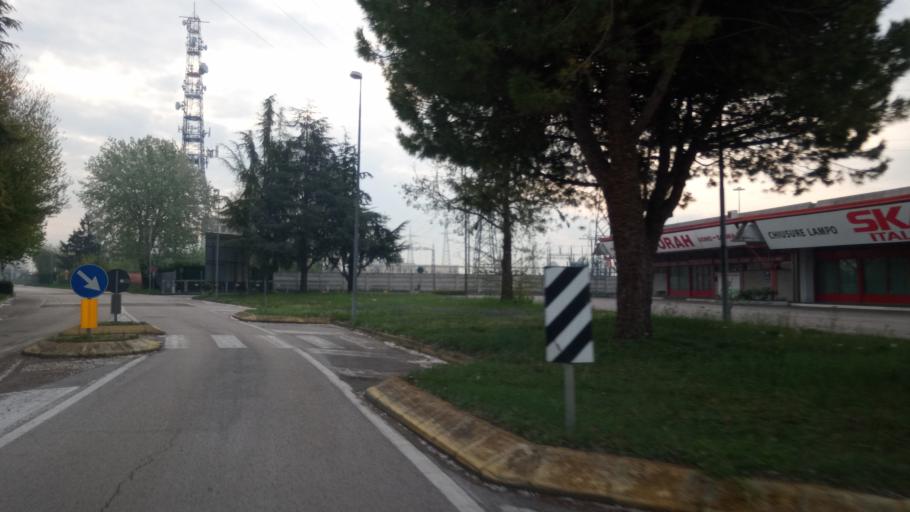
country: IT
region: Veneto
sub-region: Provincia di Padova
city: Villatora
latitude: 45.3891
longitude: 11.9472
